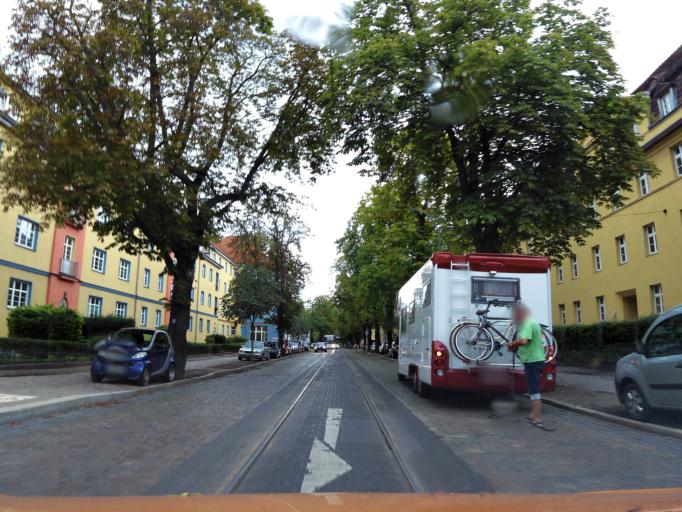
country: DE
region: Brandenburg
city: Potsdam
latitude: 52.3902
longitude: 13.0281
